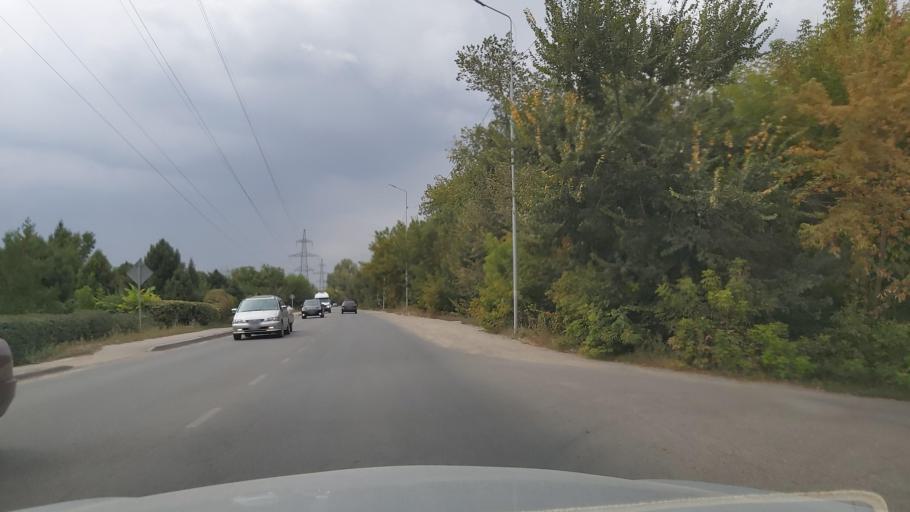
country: KZ
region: Almaty Oblysy
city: Energeticheskiy
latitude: 43.4044
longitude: 77.0240
